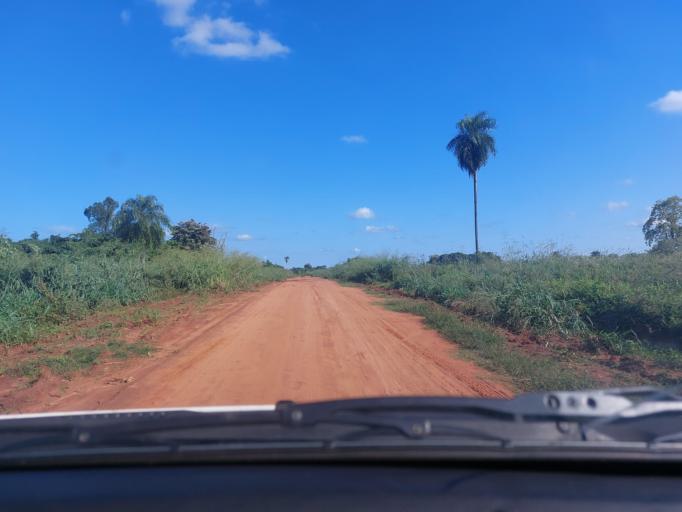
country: PY
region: San Pedro
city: Guayaybi
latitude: -24.5200
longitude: -56.5463
